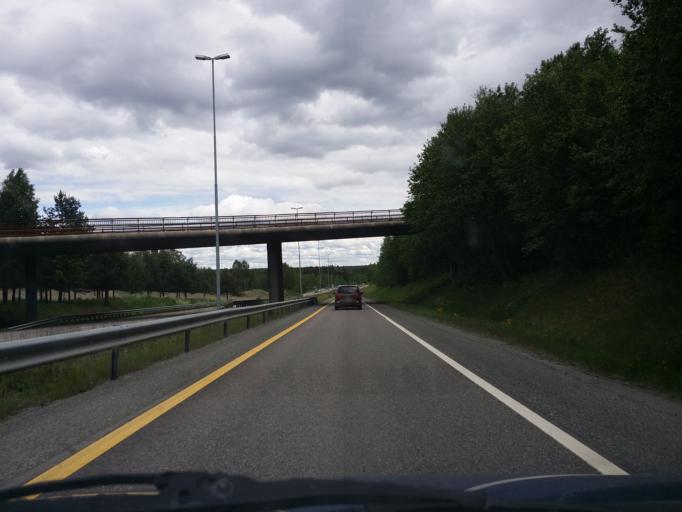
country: NO
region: Hedmark
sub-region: Hamar
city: Hamar
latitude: 60.8420
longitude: 11.0485
